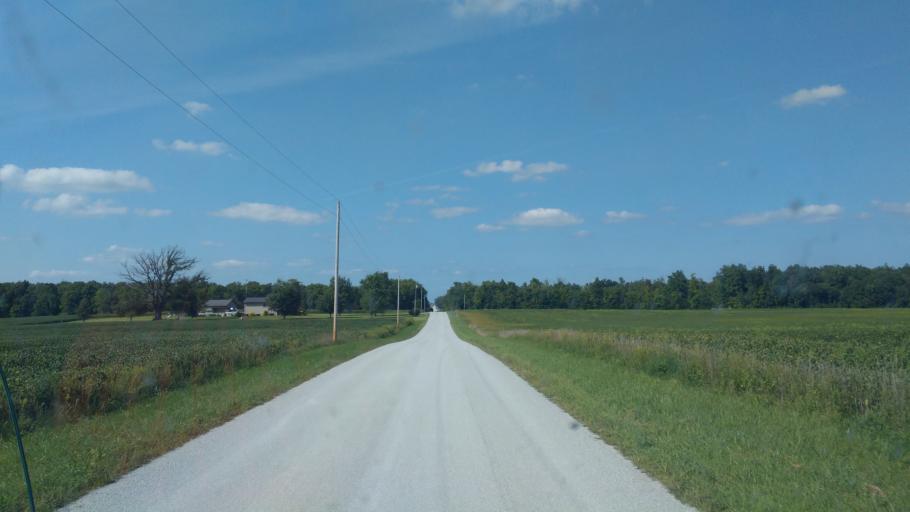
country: US
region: Ohio
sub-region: Hardin County
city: Forest
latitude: 40.6477
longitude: -83.4390
